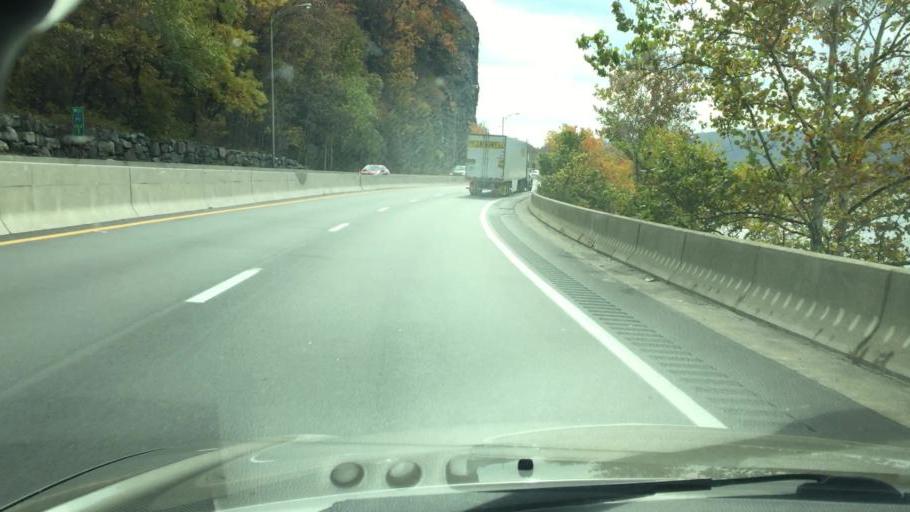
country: US
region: Pennsylvania
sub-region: Monroe County
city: East Stroudsburg
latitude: 40.9692
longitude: -75.1195
